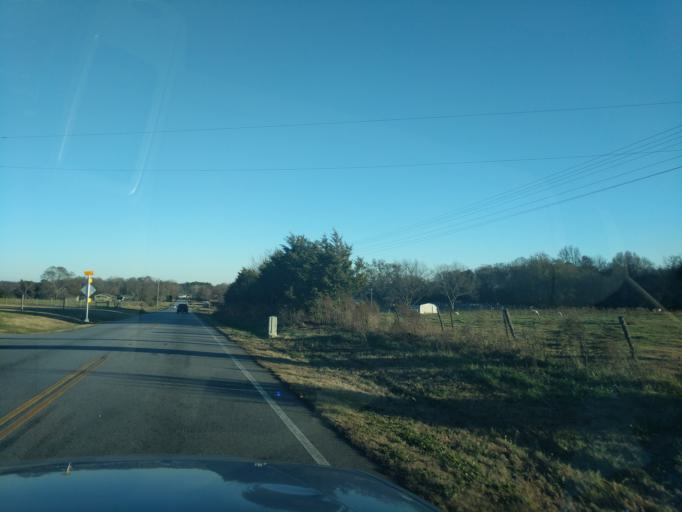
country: US
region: South Carolina
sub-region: Oconee County
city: Westminster
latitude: 34.6003
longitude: -83.0152
